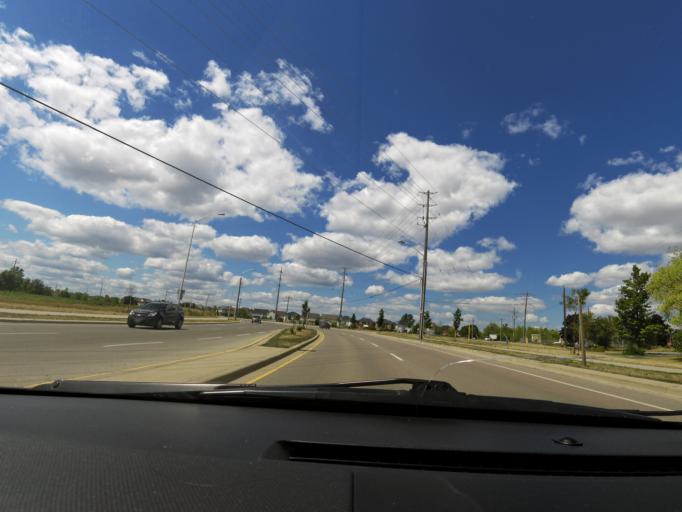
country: CA
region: Ontario
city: Burlington
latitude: 43.4071
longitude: -79.7729
